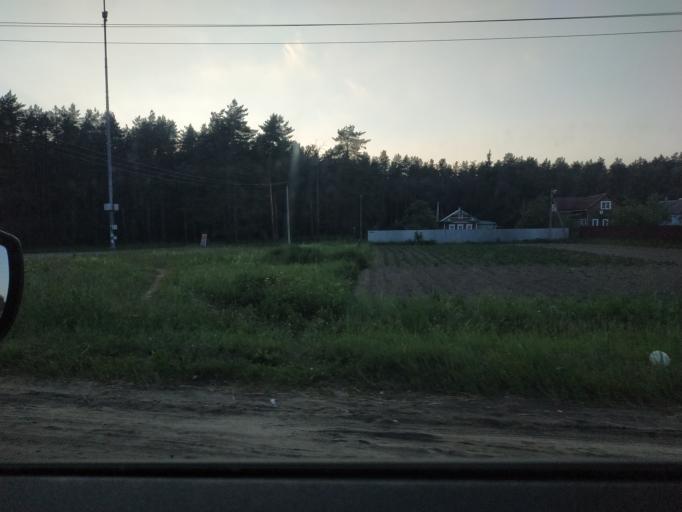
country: RU
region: Moskovskaya
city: Krasnoarmeysk
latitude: 56.0556
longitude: 38.2397
